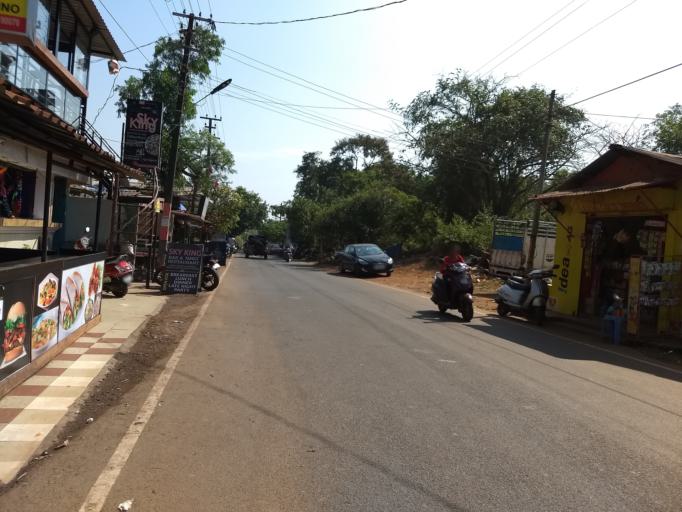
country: IN
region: Goa
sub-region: North Goa
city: Vagator
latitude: 15.5987
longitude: 73.7431
